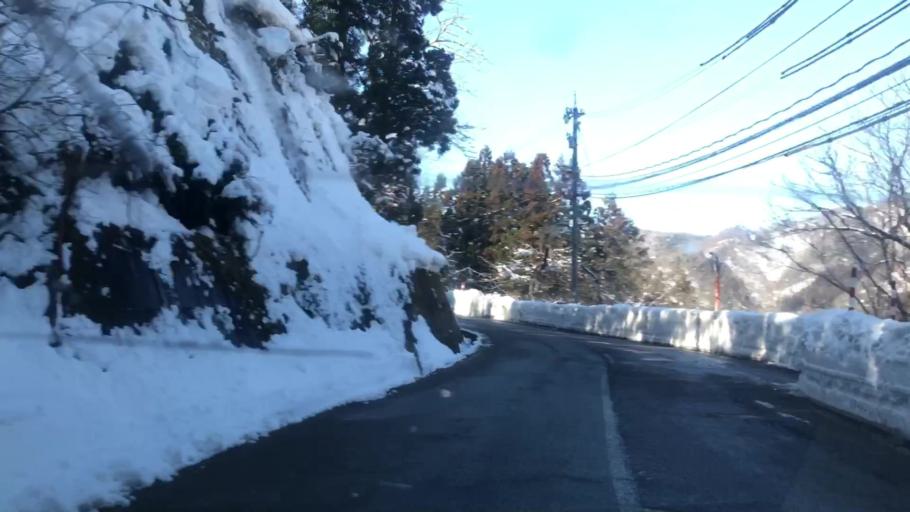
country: JP
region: Toyama
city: Kamiichi
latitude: 36.5688
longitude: 137.3632
